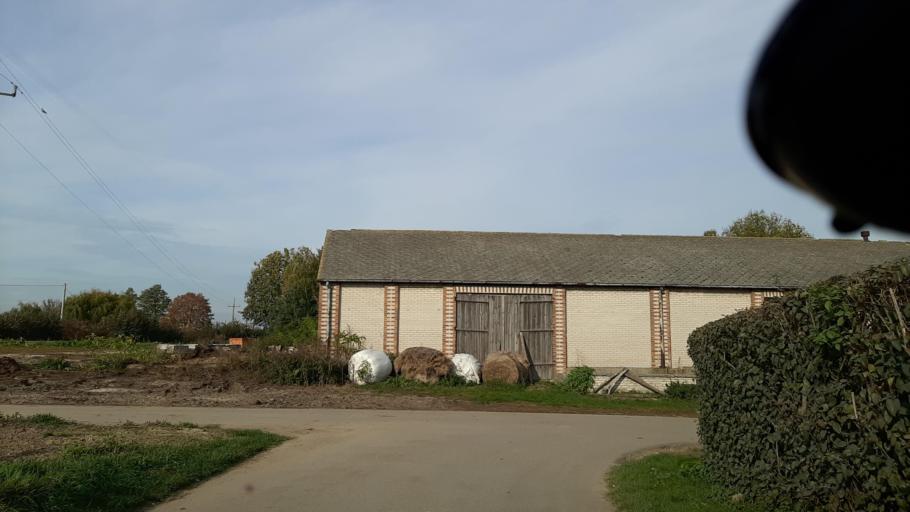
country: PL
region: Lublin Voivodeship
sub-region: Powiat lubelski
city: Jastkow
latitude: 51.3413
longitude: 22.4097
